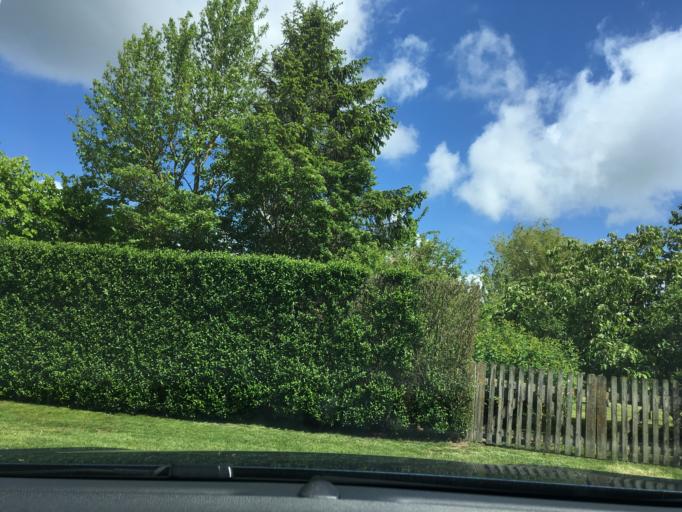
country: BE
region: Flanders
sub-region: Provincie West-Vlaanderen
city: Hooglede
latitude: 50.9923
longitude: 3.0959
